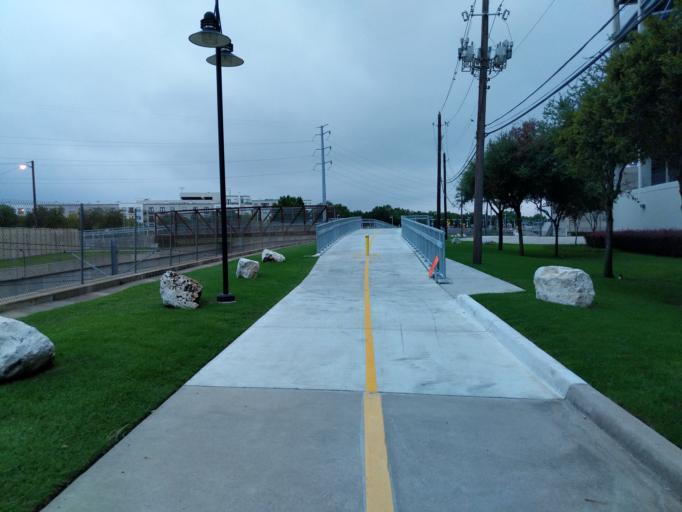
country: US
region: Texas
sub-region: Dallas County
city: Highland Park
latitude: 32.8399
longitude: -96.7733
